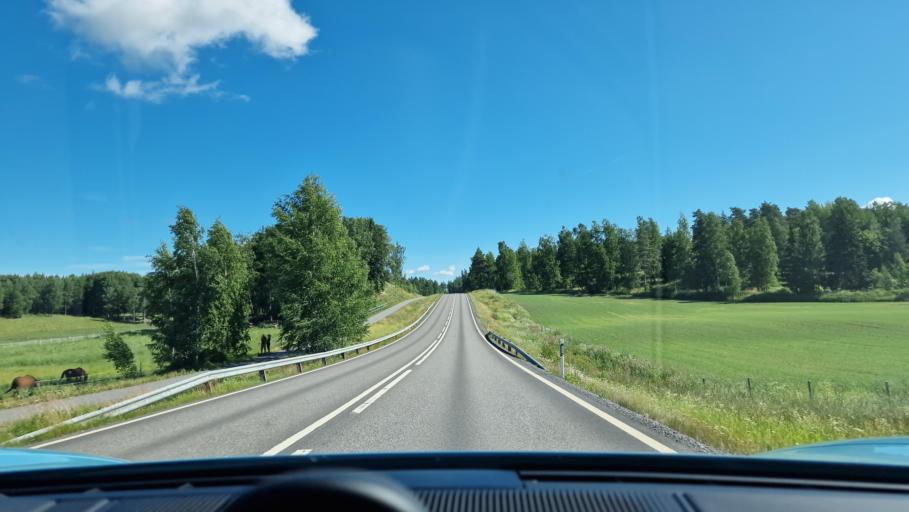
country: FI
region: Pirkanmaa
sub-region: Tampere
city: Kangasala
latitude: 61.4780
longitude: 24.1435
